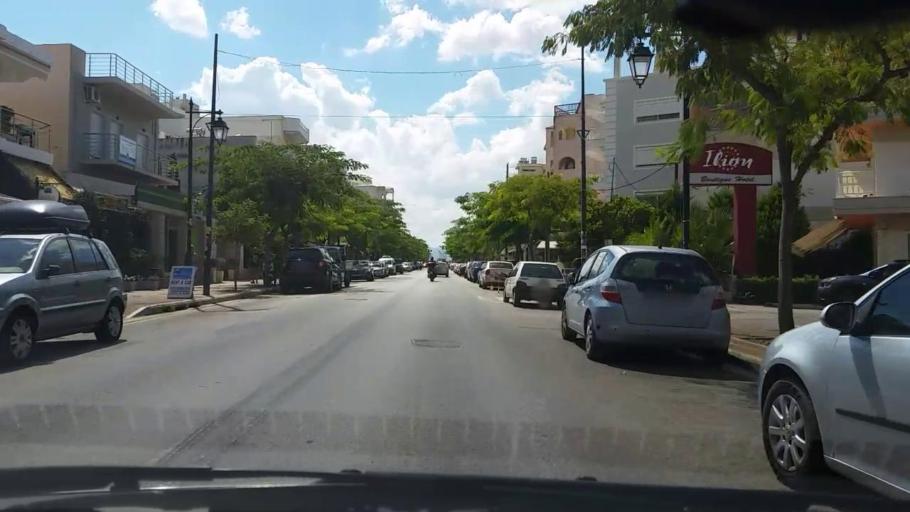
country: GR
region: Peloponnese
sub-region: Nomos Korinthias
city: Loutraki
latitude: 37.9718
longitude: 22.9778
